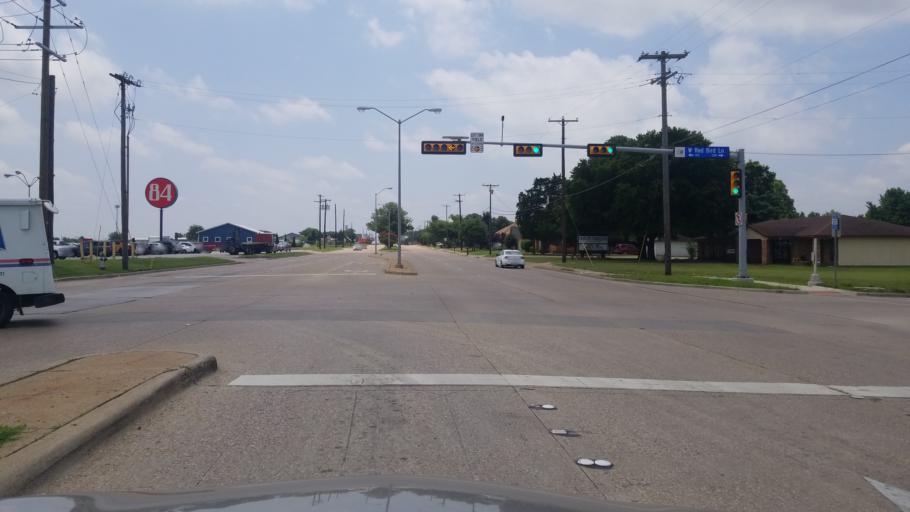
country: US
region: Texas
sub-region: Dallas County
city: Duncanville
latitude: 32.6748
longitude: -96.9086
